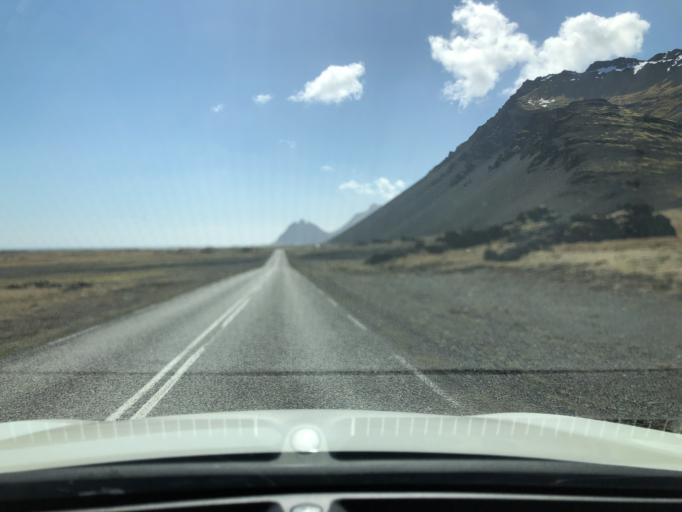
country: IS
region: East
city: Hoefn
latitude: 64.3721
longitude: -14.9236
